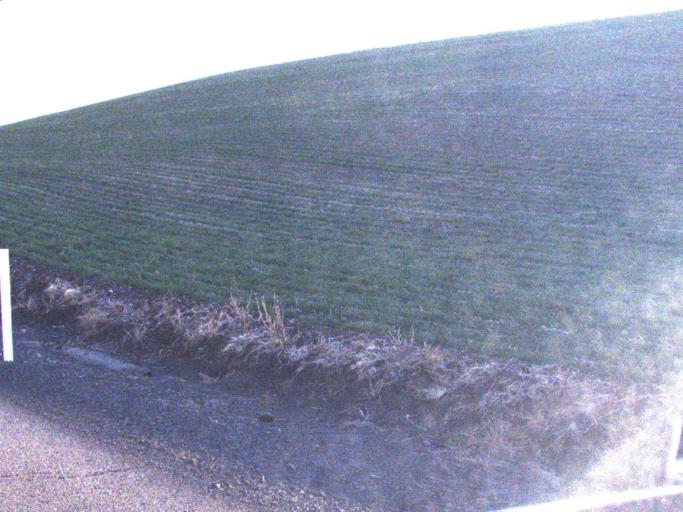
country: US
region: Washington
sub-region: Garfield County
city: Pomeroy
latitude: 46.7107
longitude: -117.7818
